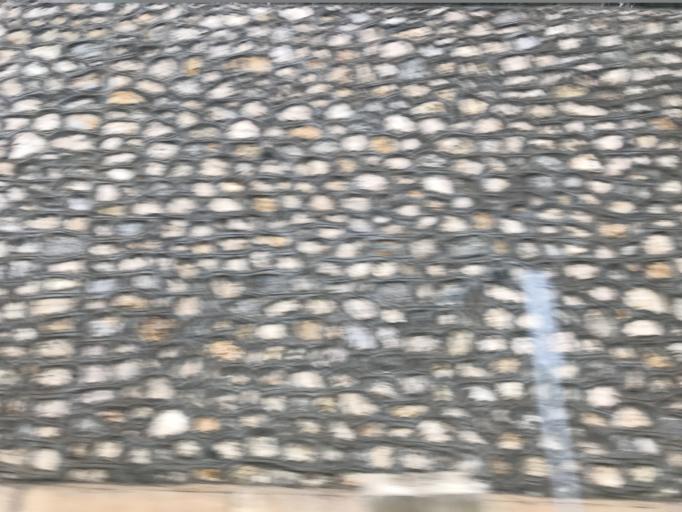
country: TR
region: Bartin
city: Amasra
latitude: 41.7337
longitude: 32.3758
